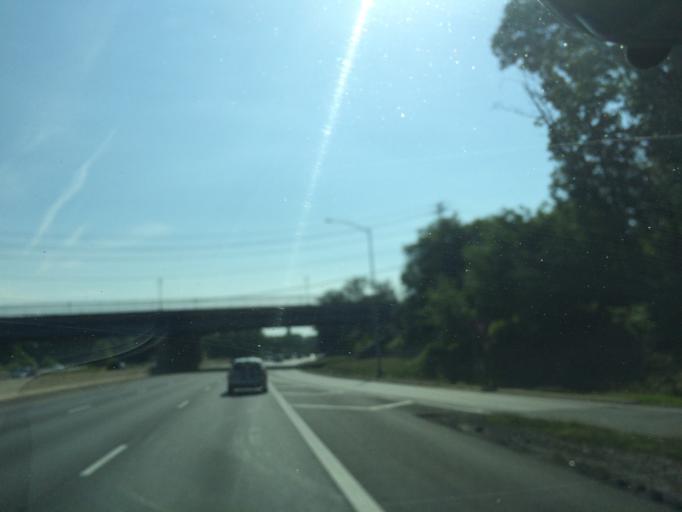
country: US
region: Maryland
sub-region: Baltimore County
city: Lutherville
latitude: 39.4134
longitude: -76.6135
